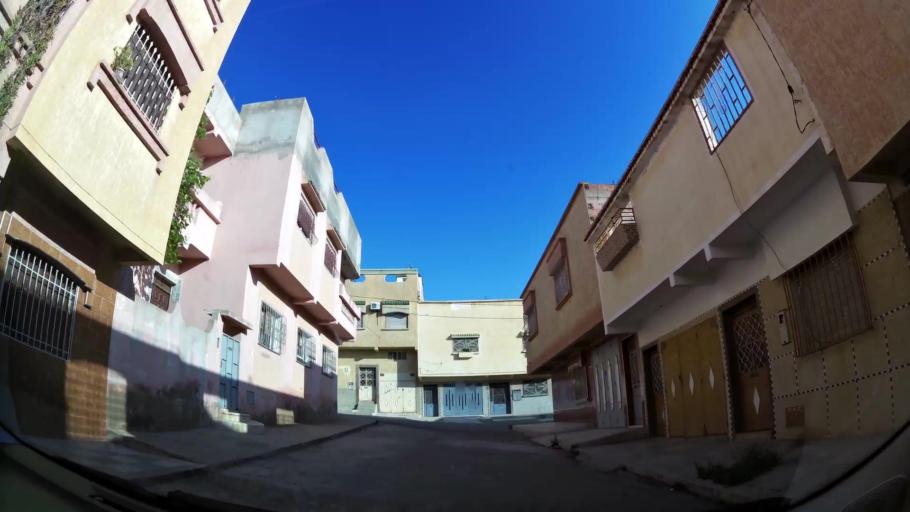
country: MA
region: Oriental
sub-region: Oujda-Angad
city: Oujda
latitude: 34.6725
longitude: -1.9442
